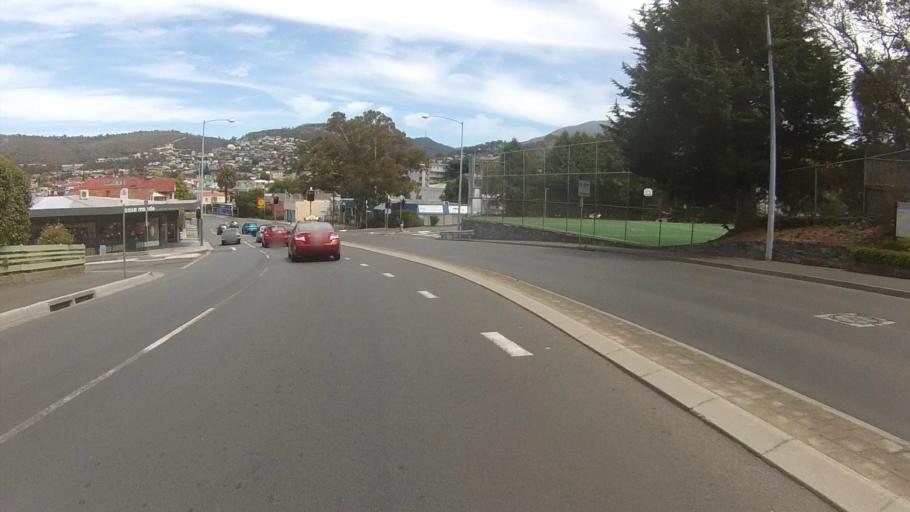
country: AU
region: Tasmania
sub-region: Hobart
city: Sandy Bay
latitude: -42.8917
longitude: 147.3268
